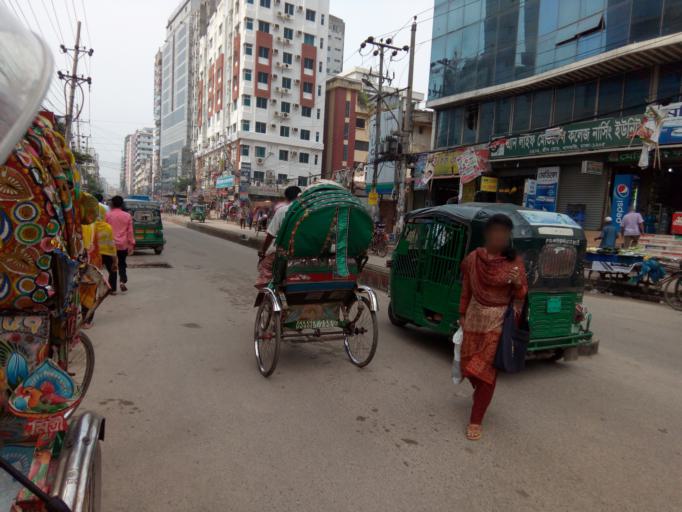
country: BD
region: Dhaka
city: Azimpur
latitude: 23.7454
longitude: 90.3850
